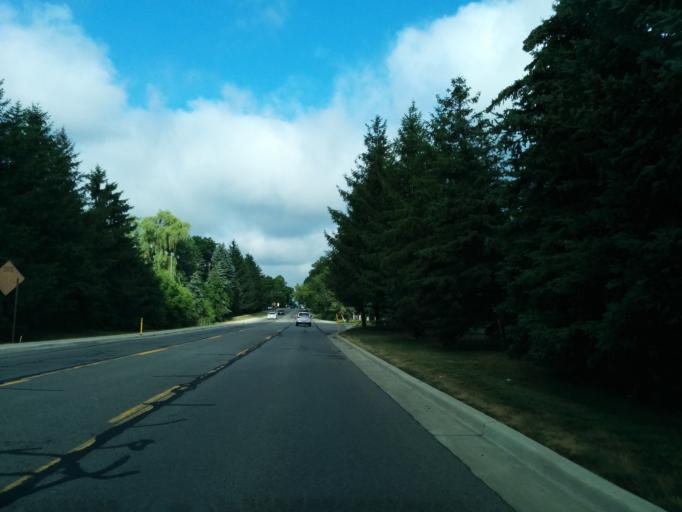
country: US
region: Michigan
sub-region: Oakland County
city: West Bloomfield Township
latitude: 42.5272
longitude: -83.4024
